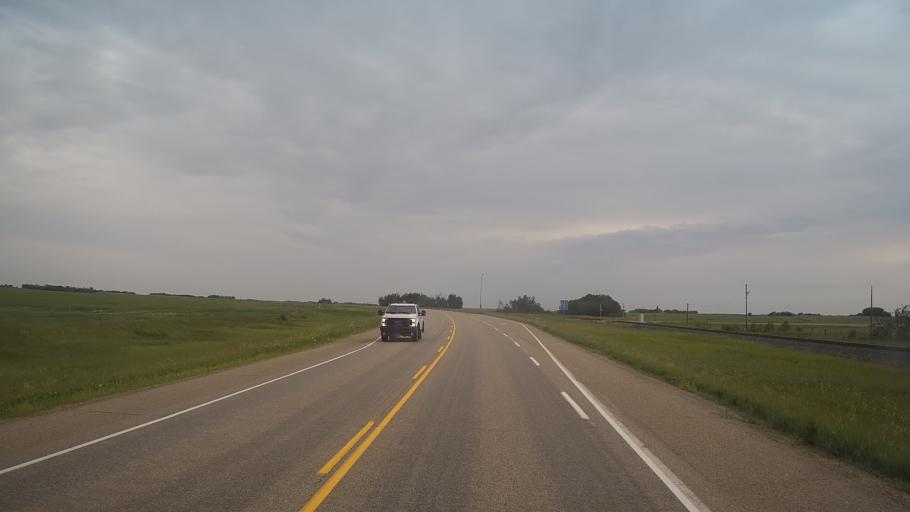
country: CA
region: Saskatchewan
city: Langham
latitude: 52.1263
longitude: -107.2861
